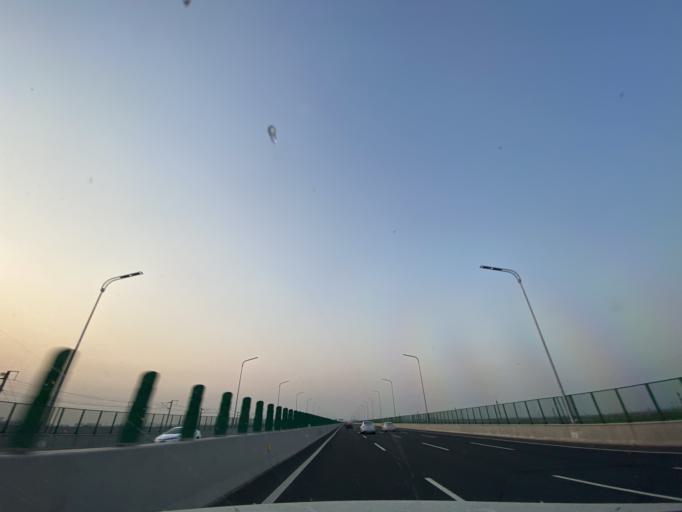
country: CN
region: Beijing
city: Weishanzhuang
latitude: 39.6704
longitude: 116.3662
